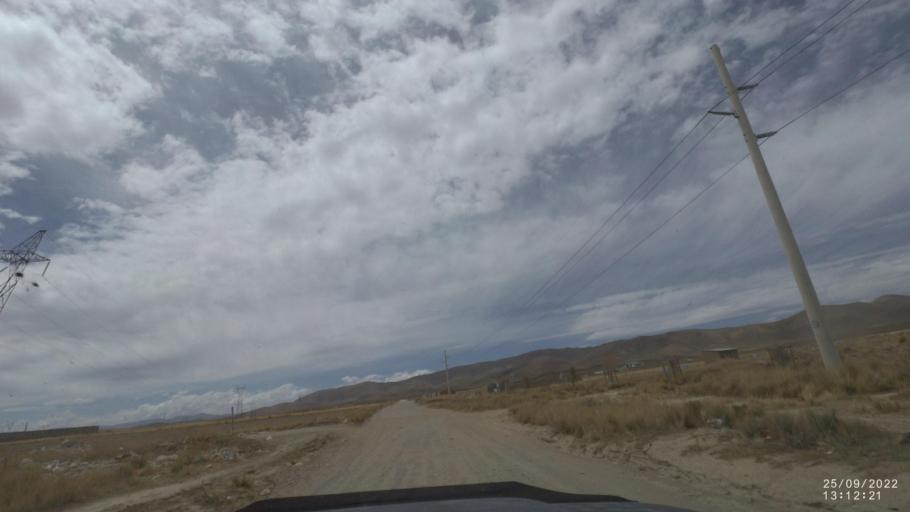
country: BO
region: Oruro
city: Oruro
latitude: -17.9577
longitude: -67.0414
